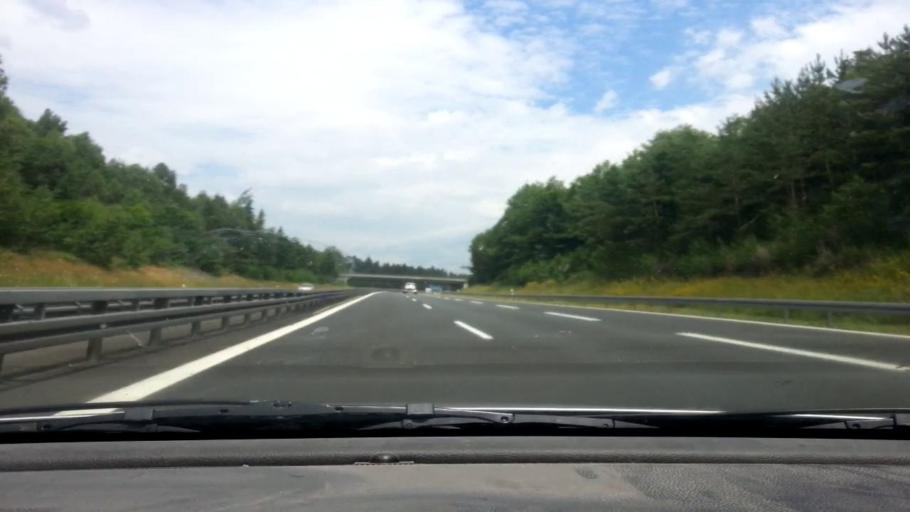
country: DE
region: Bavaria
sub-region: Upper Palatinate
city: Wiesau
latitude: 49.9084
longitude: 12.2206
